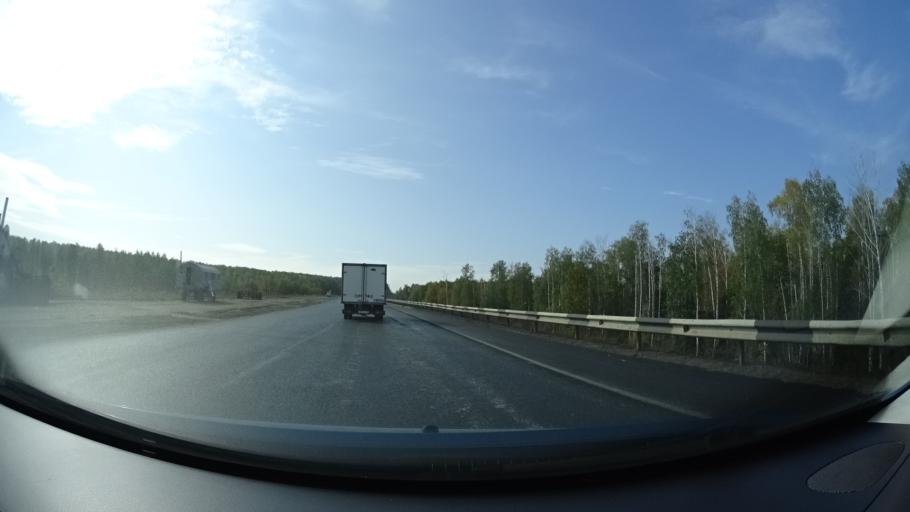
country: RU
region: Bashkortostan
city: Kandry
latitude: 54.5960
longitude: 54.2833
